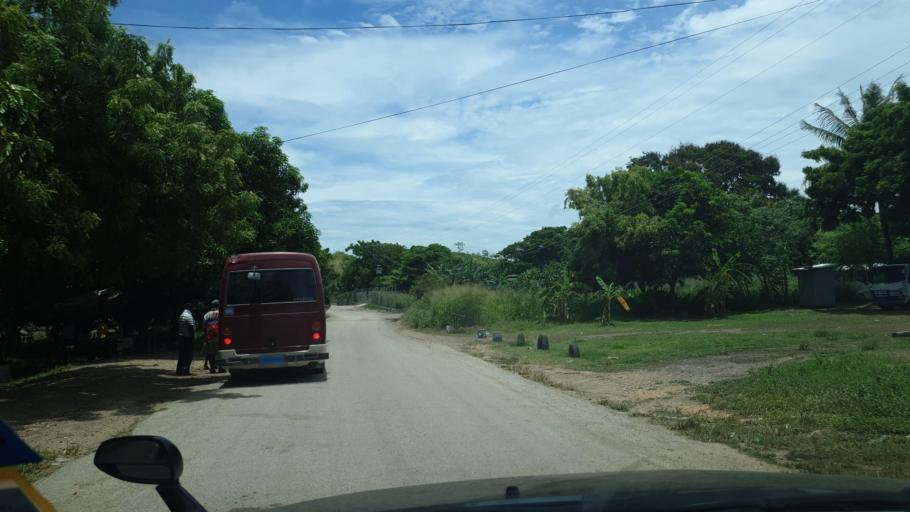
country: PG
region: National Capital
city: Port Moresby
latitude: -9.4244
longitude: 147.0497
